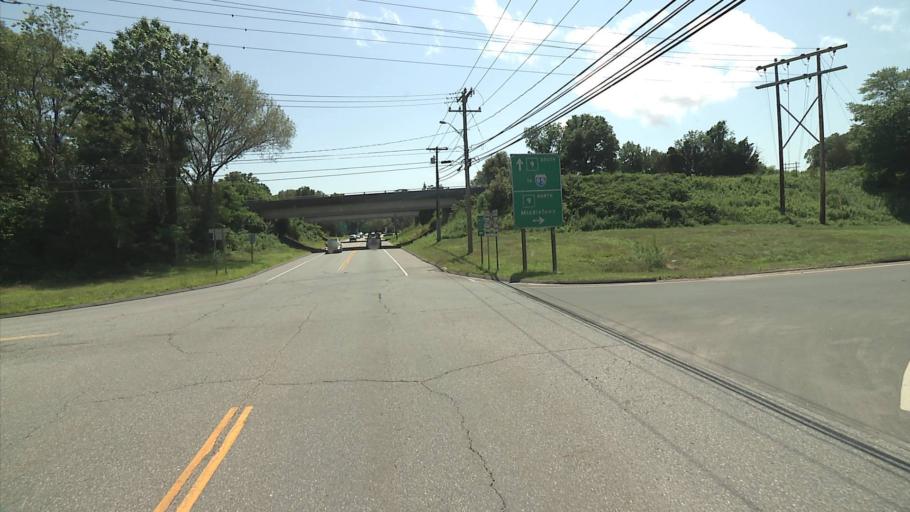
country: US
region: Connecticut
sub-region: Middlesex County
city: Old Saybrook
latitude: 41.3238
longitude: -72.3781
